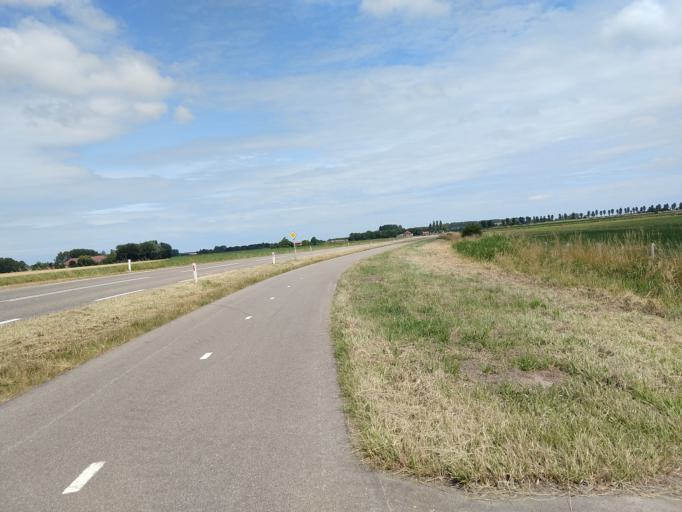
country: NL
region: Zeeland
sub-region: Gemeente Goes
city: Goes
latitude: 51.5149
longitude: 3.8261
